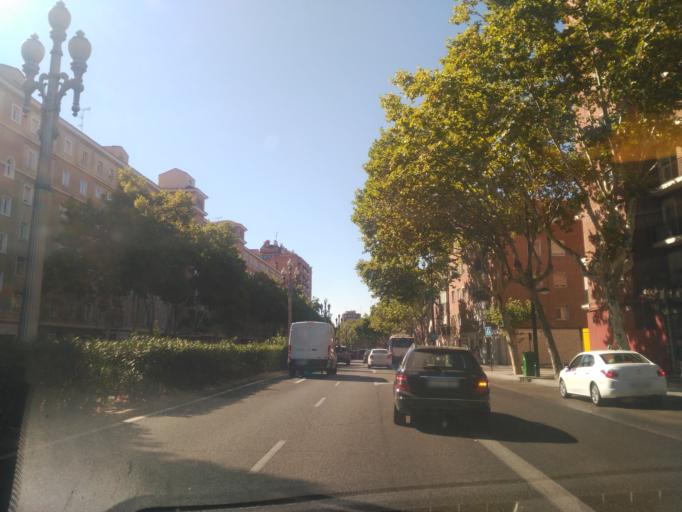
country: ES
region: Castille and Leon
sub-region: Provincia de Valladolid
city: Valladolid
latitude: 41.6369
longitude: -4.7392
